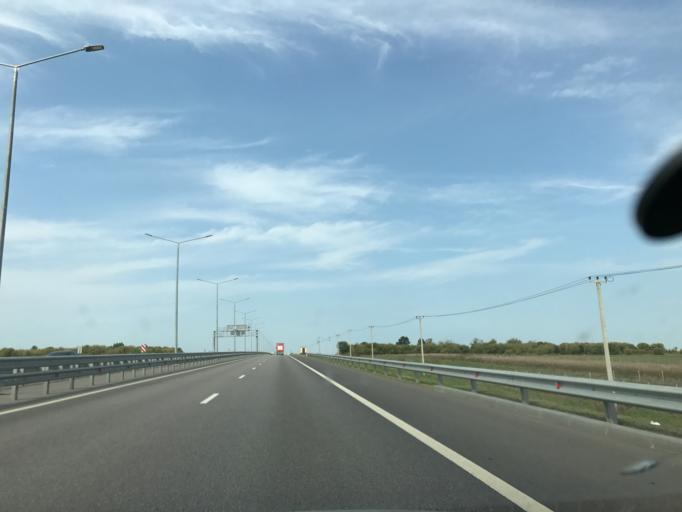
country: RU
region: Voronezj
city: Kashirskoye
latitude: 51.4945
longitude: 39.5276
